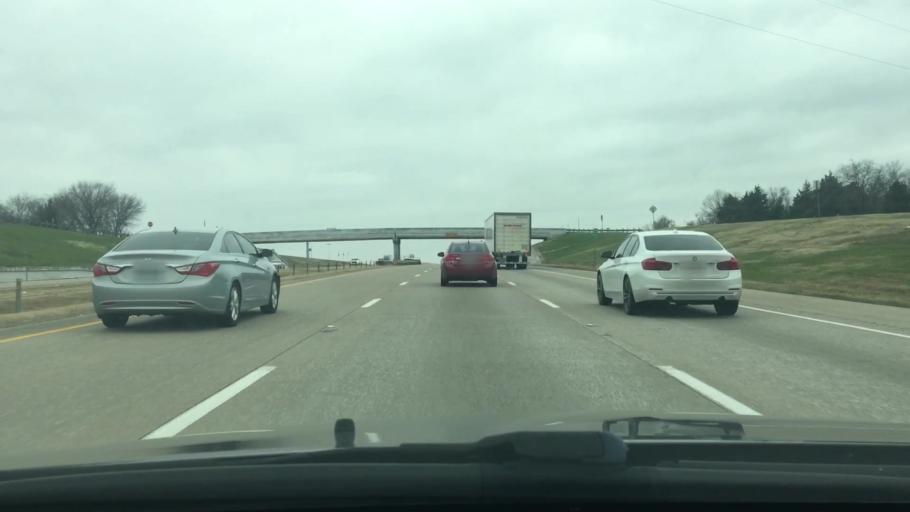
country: US
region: Texas
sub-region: Ellis County
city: Ferris
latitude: 32.4991
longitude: -96.6639
